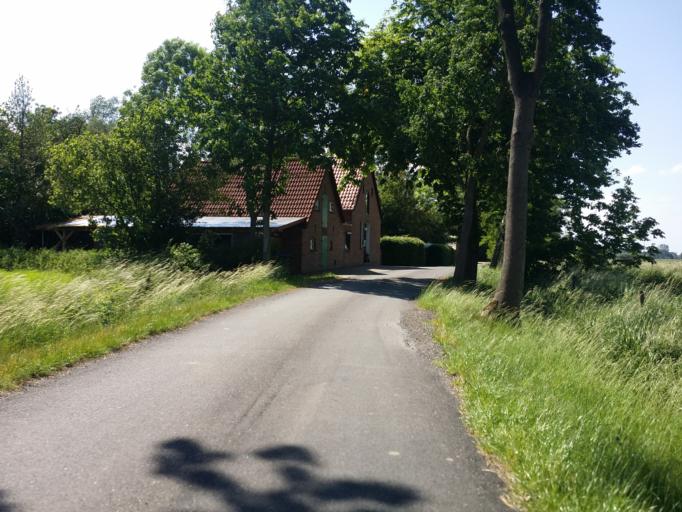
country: DE
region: Lower Saxony
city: Neuenkirchen
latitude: 53.1595
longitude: 8.5351
